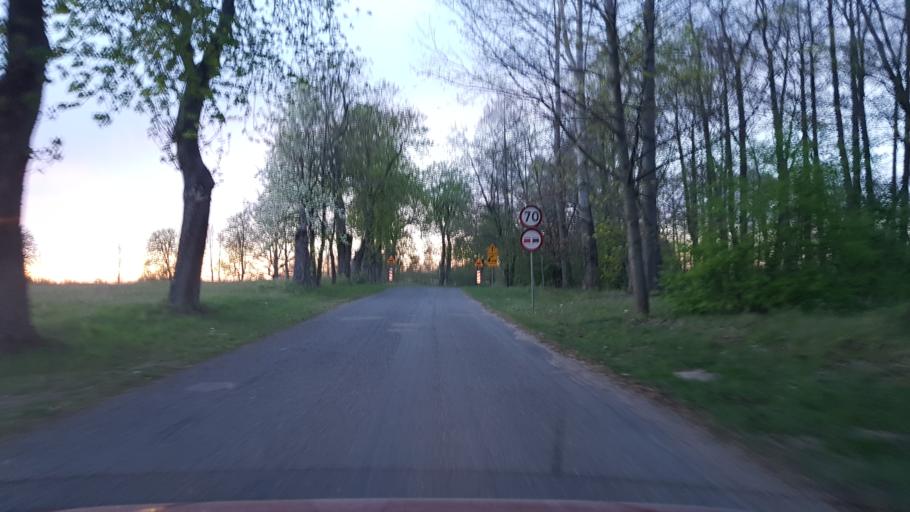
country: PL
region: West Pomeranian Voivodeship
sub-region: Powiat lobeski
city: Wegorzyno
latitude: 53.5094
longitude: 15.4490
